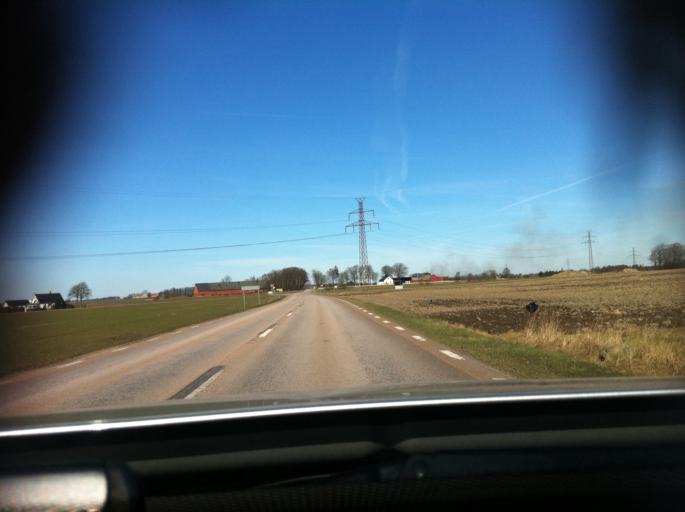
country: SE
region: Skane
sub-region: Landskrona
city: Asmundtorp
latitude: 55.9692
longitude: 12.9415
